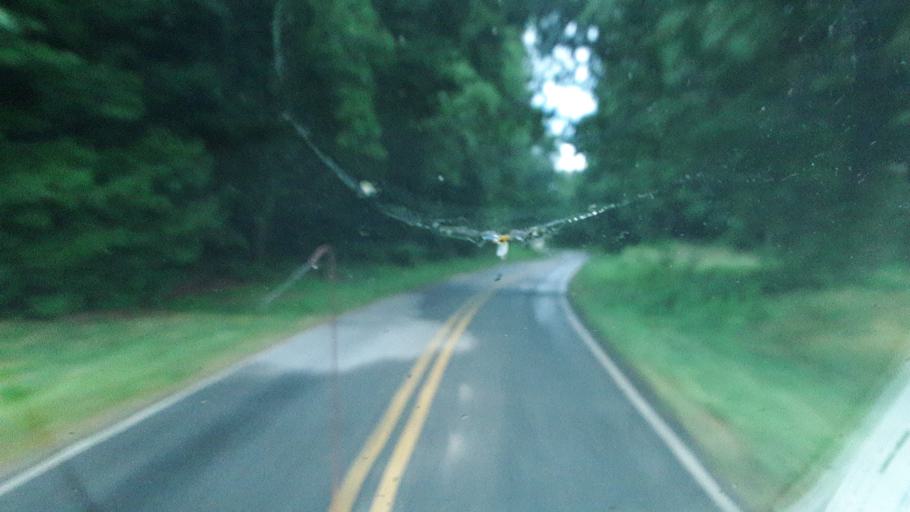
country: US
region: North Carolina
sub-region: Yadkin County
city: Jonesville
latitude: 36.1072
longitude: -80.8822
